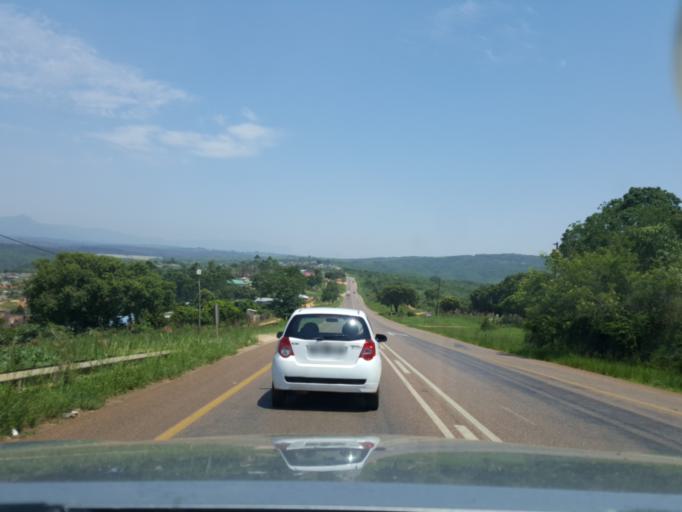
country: ZA
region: Limpopo
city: Thulamahashi
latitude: -24.9117
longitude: 31.1171
